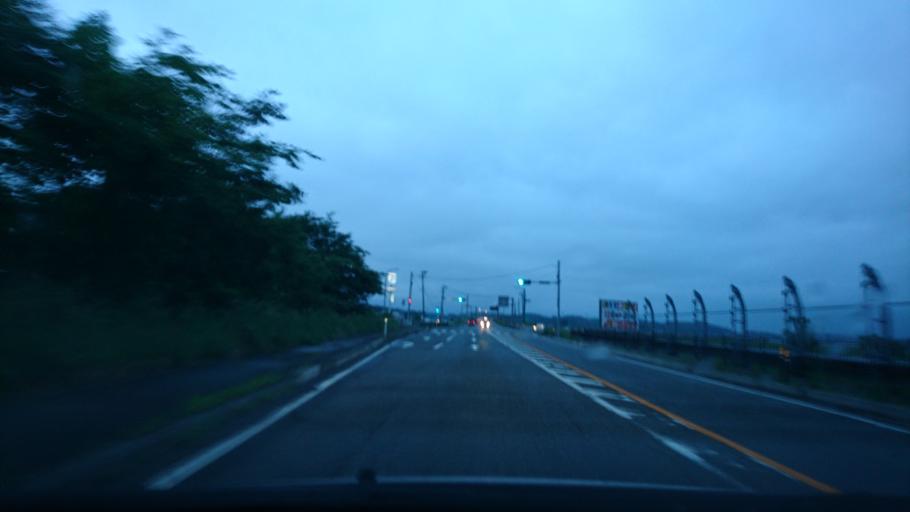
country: JP
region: Iwate
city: Ichinoseki
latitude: 38.8040
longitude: 141.0666
